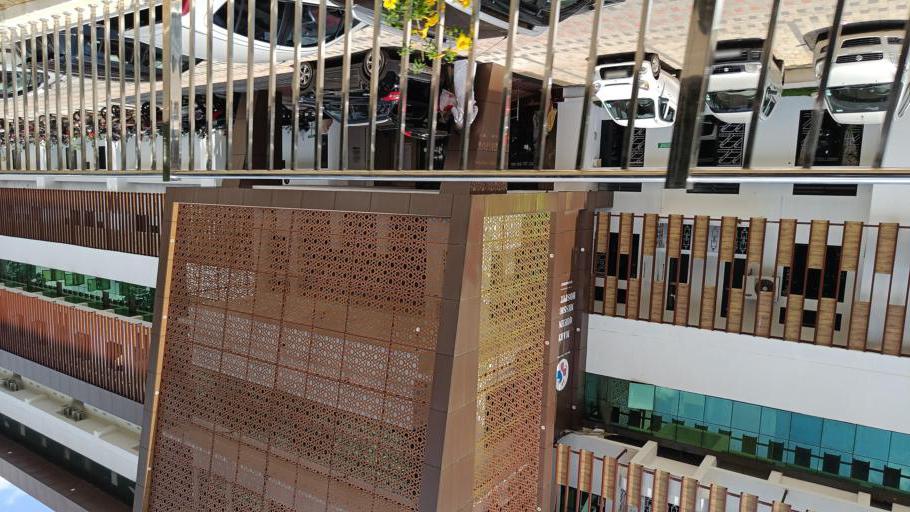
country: IN
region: Kerala
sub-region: Kottayam
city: Erattupetta
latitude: 9.5582
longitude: 76.8134
